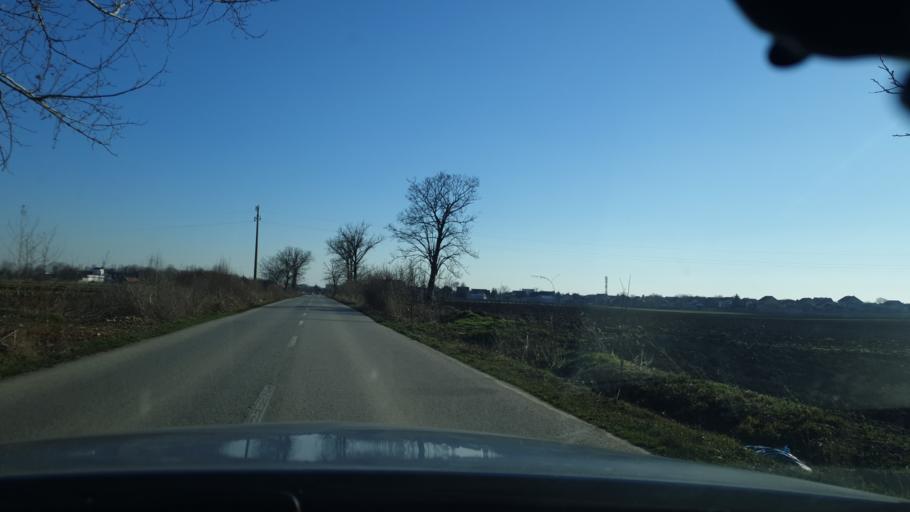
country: RS
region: Autonomna Pokrajina Vojvodina
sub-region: Sremski Okrug
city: Ruma
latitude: 45.0241
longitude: 19.8136
